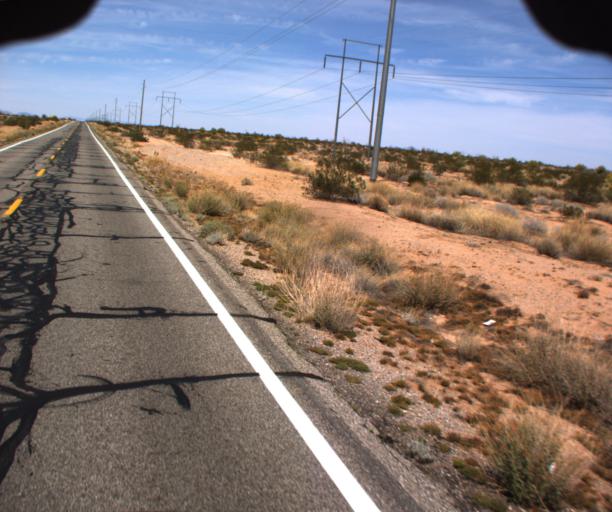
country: US
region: Arizona
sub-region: La Paz County
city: Quartzsite
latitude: 33.8274
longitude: -114.2170
